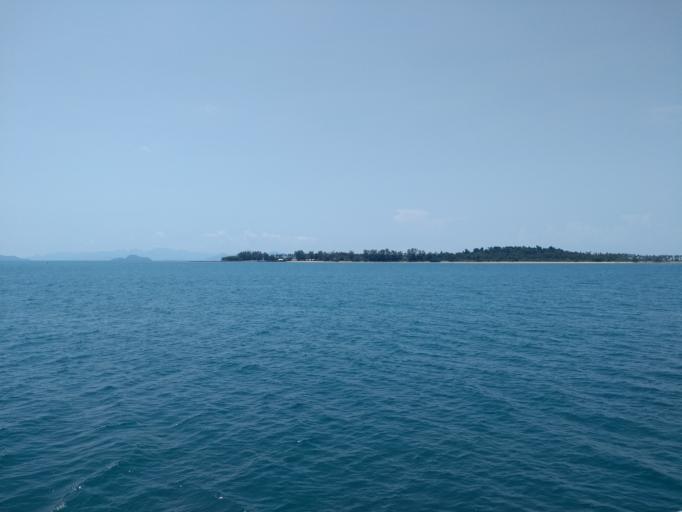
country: TH
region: Trat
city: Ko Kut
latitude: 11.8193
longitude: 102.5291
